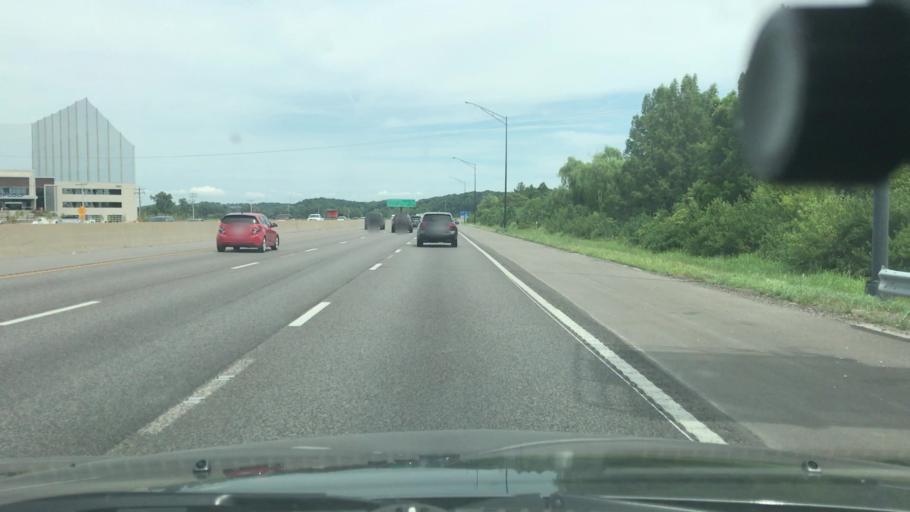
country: US
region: Missouri
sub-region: Saint Louis County
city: Chesterfield
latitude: 38.6694
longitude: -90.5864
